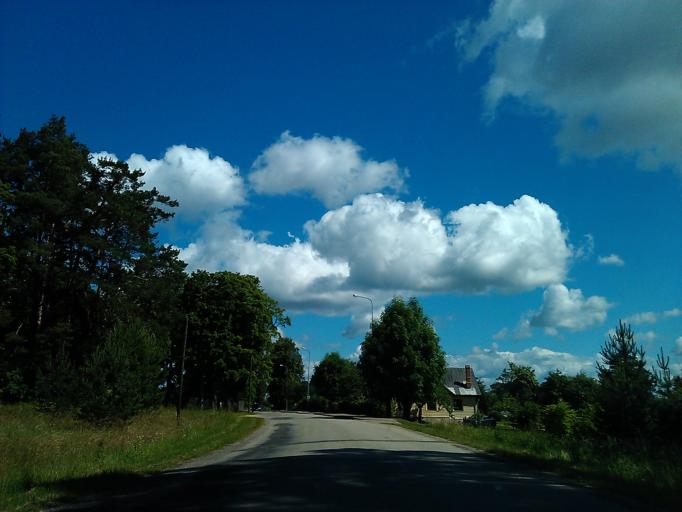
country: LV
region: Varaklani
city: Varaklani
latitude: 56.6025
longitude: 26.7359
